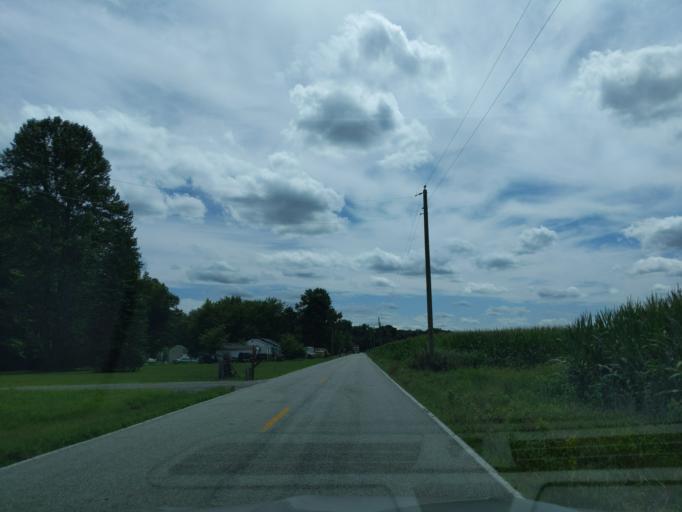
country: US
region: Indiana
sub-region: Ripley County
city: Batesville
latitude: 39.2209
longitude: -85.2680
